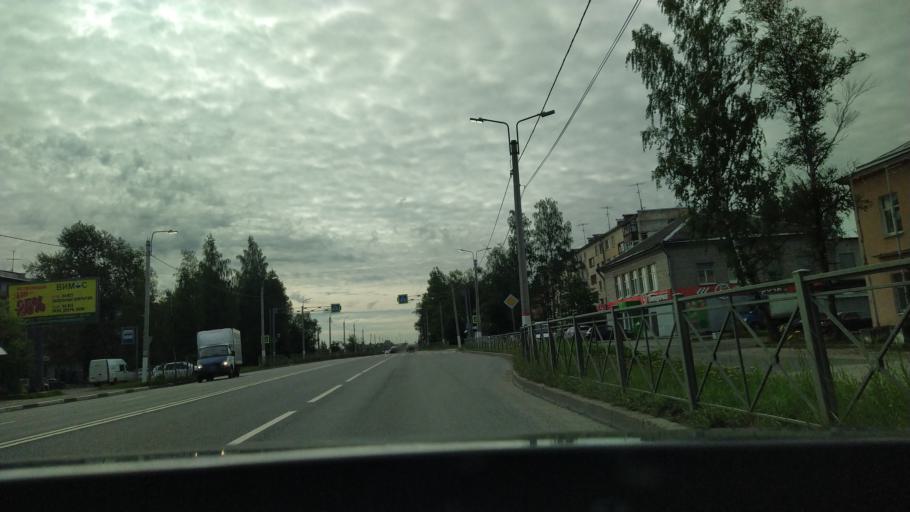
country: RU
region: Leningrad
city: Tosno
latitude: 59.5594
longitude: 30.8432
